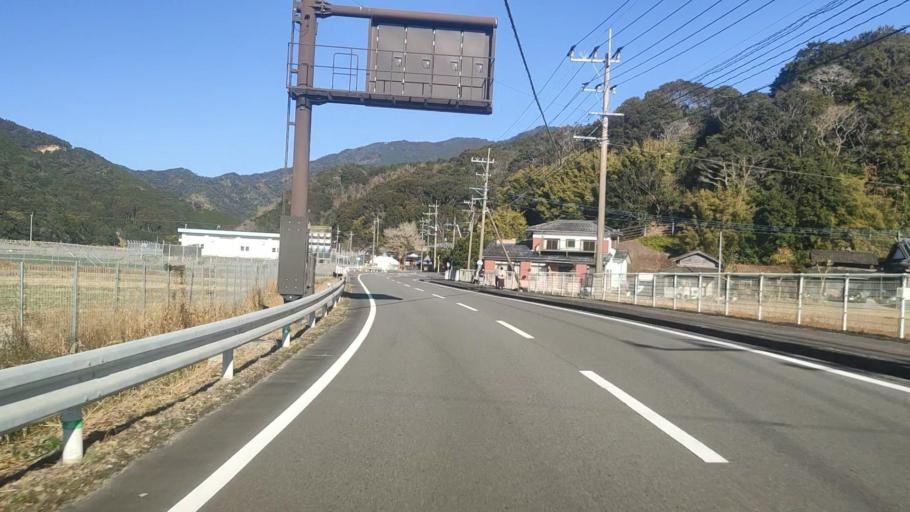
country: JP
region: Miyazaki
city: Nobeoka
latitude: 32.6666
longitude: 131.7667
